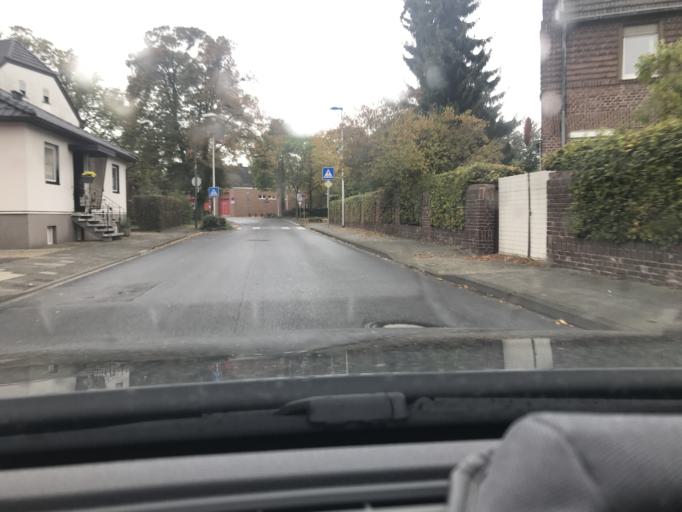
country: DE
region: North Rhine-Westphalia
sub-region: Regierungsbezirk Koln
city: Dueren
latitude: 50.8169
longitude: 6.4478
